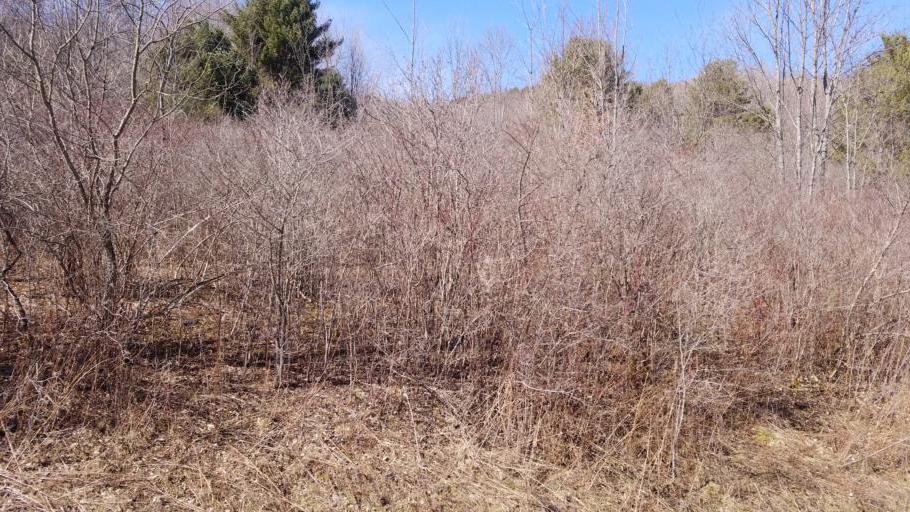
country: US
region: New York
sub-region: Allegany County
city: Wellsville
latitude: 42.0501
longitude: -77.9311
